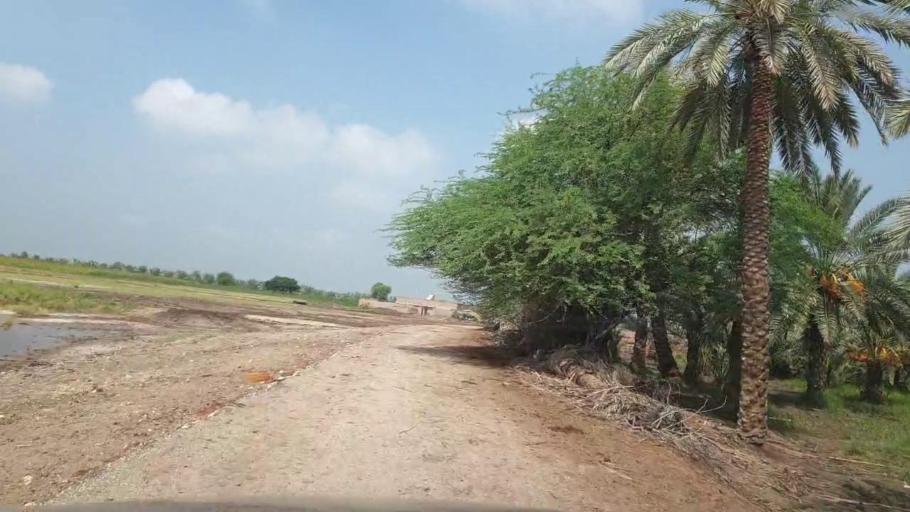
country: PK
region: Sindh
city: Pir jo Goth
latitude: 27.6046
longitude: 68.6997
